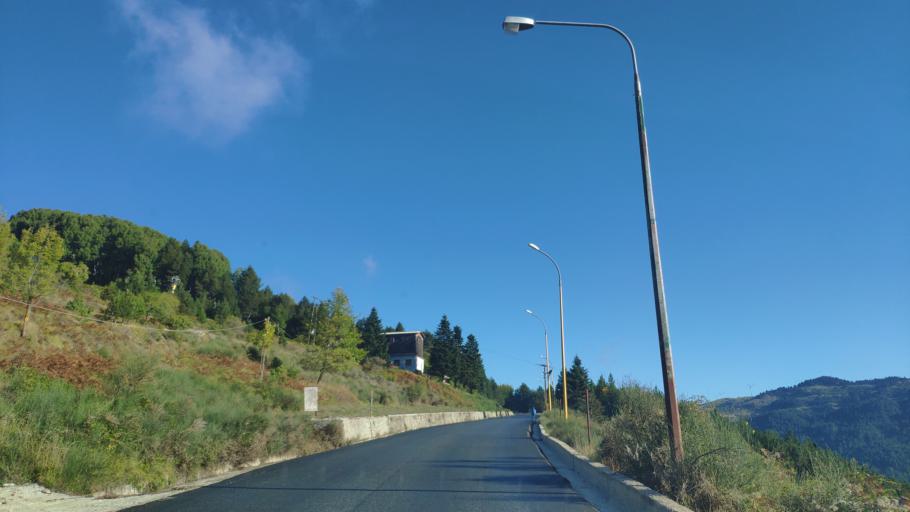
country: GR
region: Epirus
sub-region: Nomos Ioanninon
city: Metsovo
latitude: 39.7723
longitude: 21.1762
